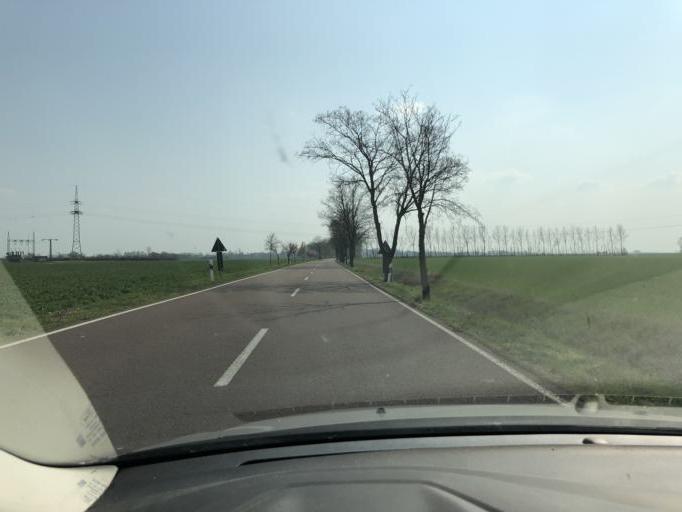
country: DE
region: Saxony-Anhalt
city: Niemberg
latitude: 51.5390
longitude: 12.0902
